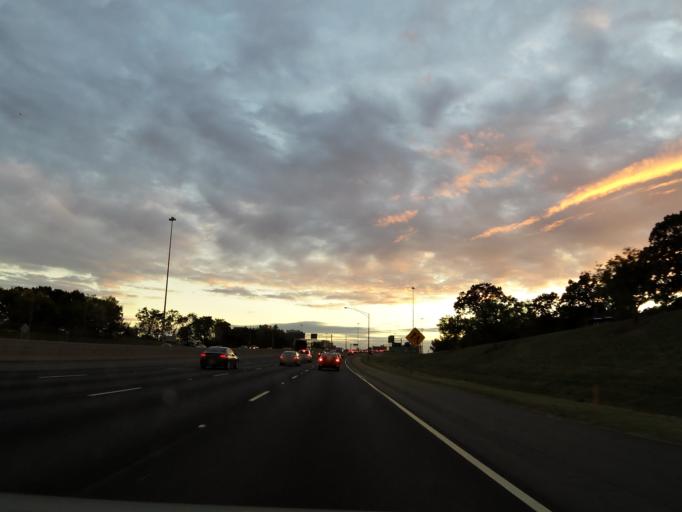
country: US
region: Alabama
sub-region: Jefferson County
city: Birmingham
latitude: 33.5330
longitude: -86.7987
